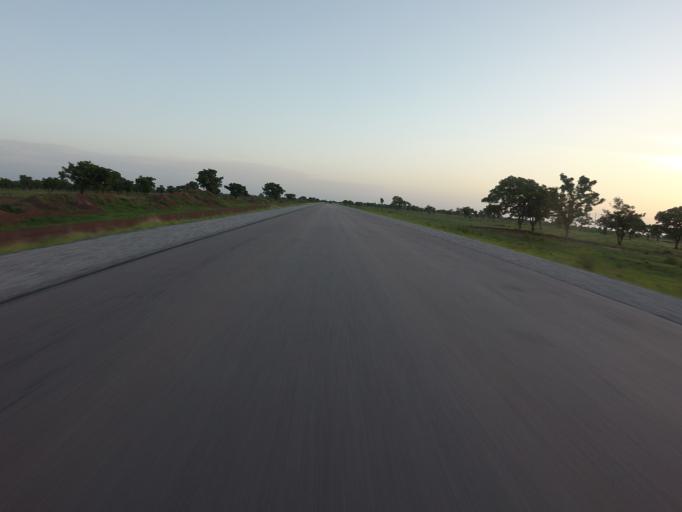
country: GH
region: Northern
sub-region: Yendi
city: Yendi
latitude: 9.9530
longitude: -0.1537
